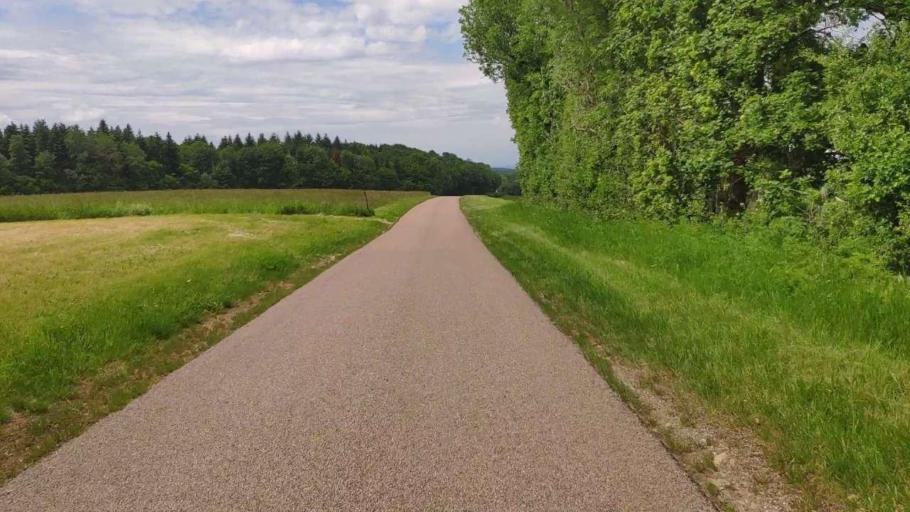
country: FR
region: Franche-Comte
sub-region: Departement du Jura
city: Poligny
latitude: 46.7787
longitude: 5.6620
